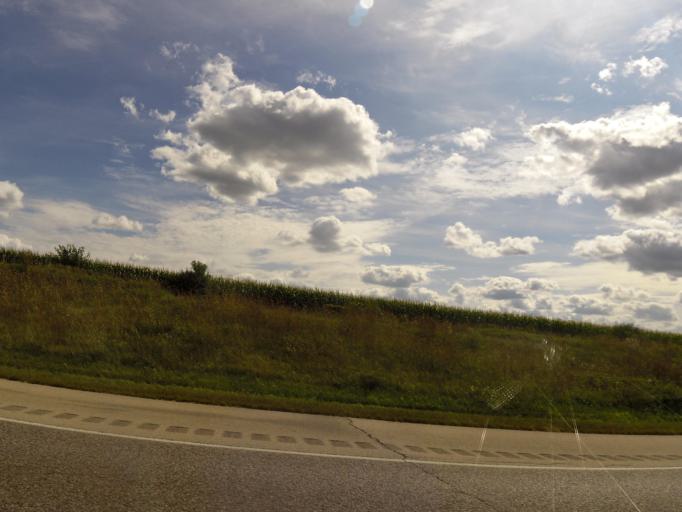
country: US
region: Illinois
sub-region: Ogle County
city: Rochelle
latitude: 41.9052
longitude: -88.9967
